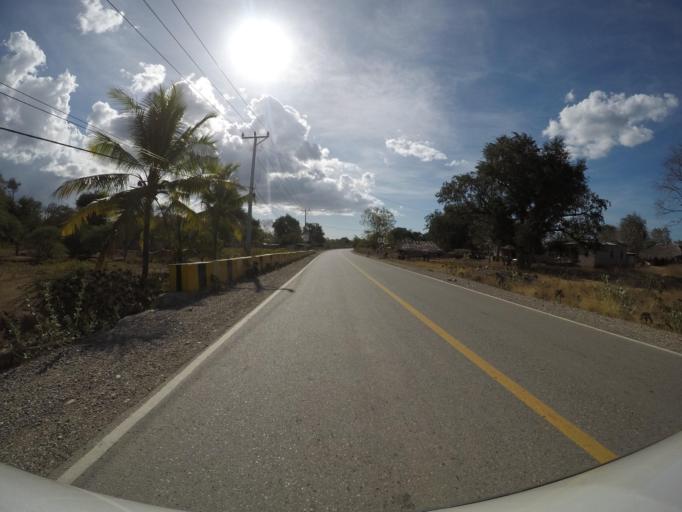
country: TL
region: Baucau
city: Baucau
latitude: -8.4834
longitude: 126.5523
